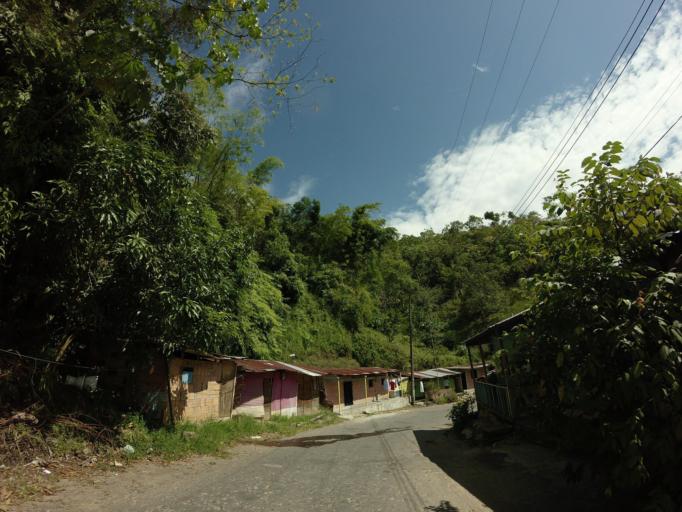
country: CO
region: Caldas
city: Norcasia
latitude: 5.5748
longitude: -74.8952
